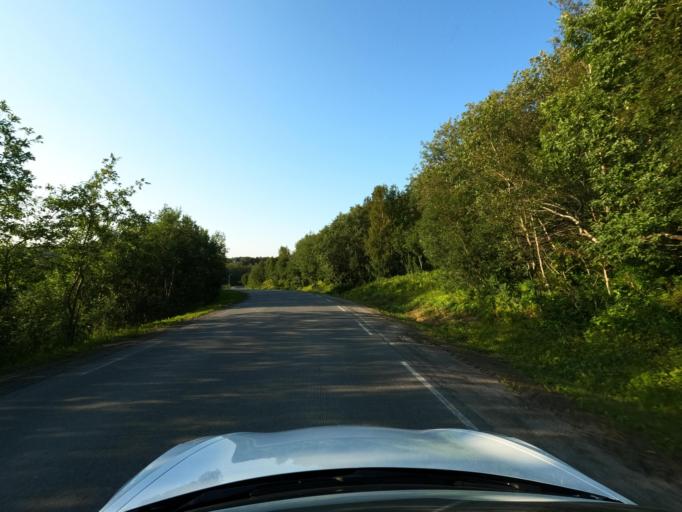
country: NO
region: Troms
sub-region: Skanland
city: Evenskjer
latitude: 68.4899
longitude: 16.7156
